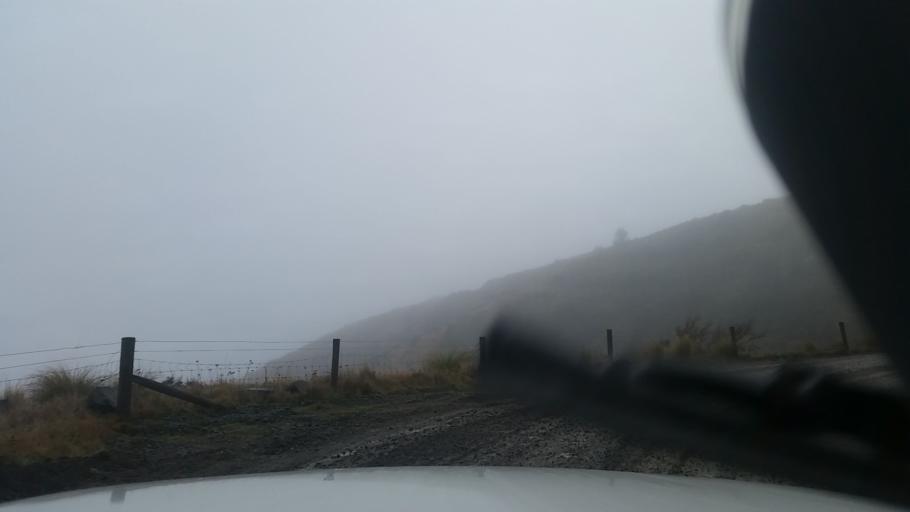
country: NZ
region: Canterbury
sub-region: Christchurch City
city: Christchurch
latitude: -43.8117
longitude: 172.8200
